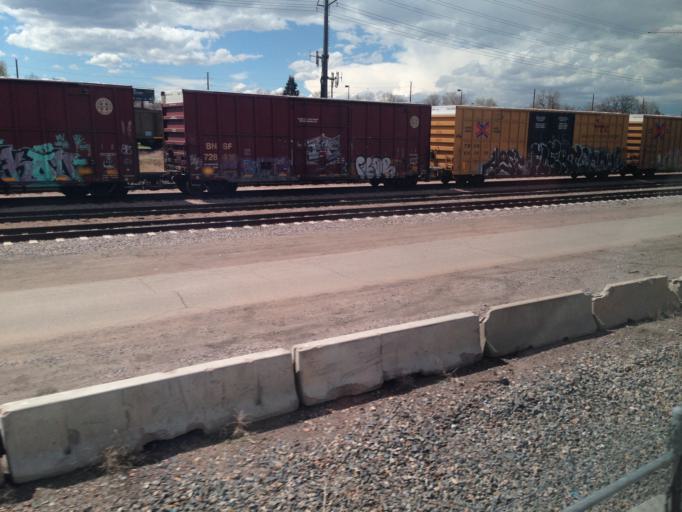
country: US
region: Colorado
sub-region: Denver County
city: Denver
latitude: 39.7688
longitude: -104.9972
